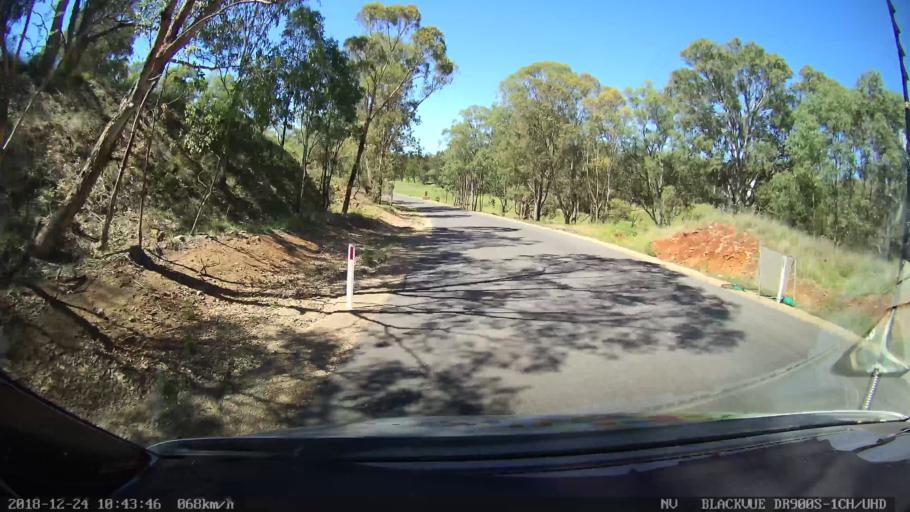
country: AU
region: New South Wales
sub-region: Upper Hunter Shire
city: Merriwa
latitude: -31.8853
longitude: 150.4441
